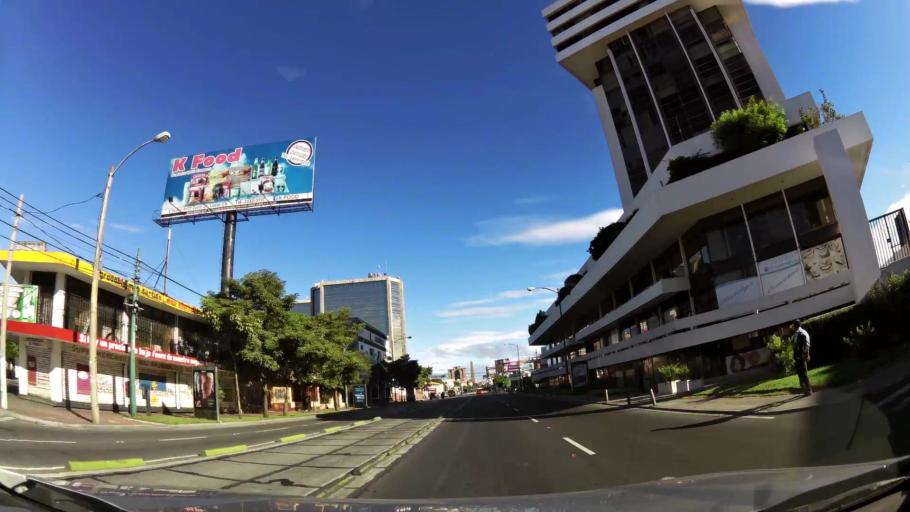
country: GT
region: Guatemala
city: Guatemala City
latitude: 14.6164
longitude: -90.5160
